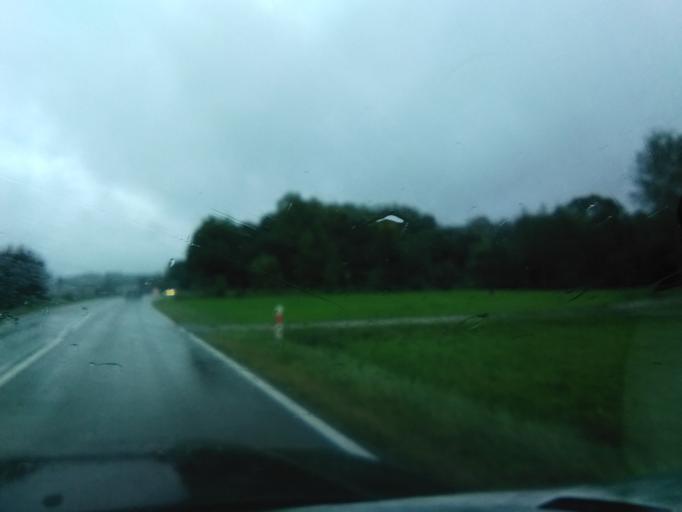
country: PL
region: Subcarpathian Voivodeship
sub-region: Powiat ropczycko-sedziszowski
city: Niedzwiada
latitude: 49.9873
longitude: 21.5613
